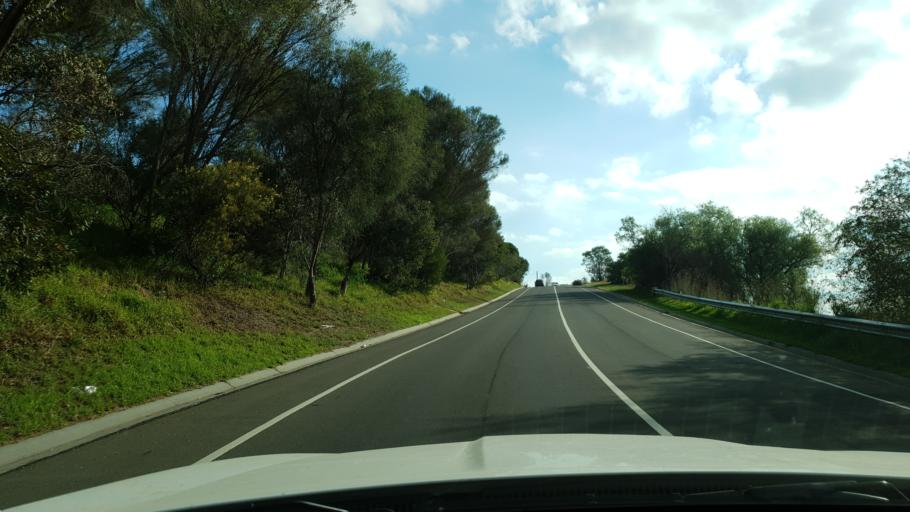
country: AU
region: Victoria
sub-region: East Gippsland
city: Bairnsdale
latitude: -37.8168
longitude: 147.6147
